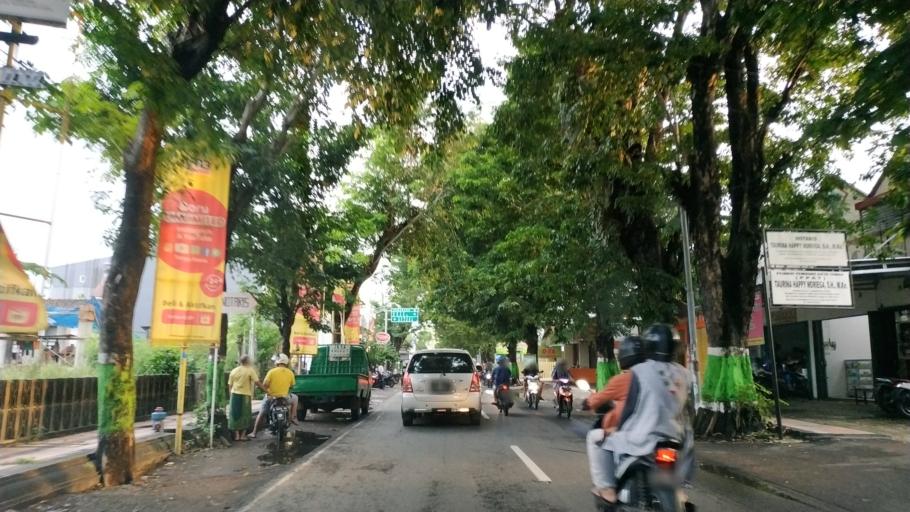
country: ID
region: Central Java
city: Kudus
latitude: -6.8108
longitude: 110.8543
